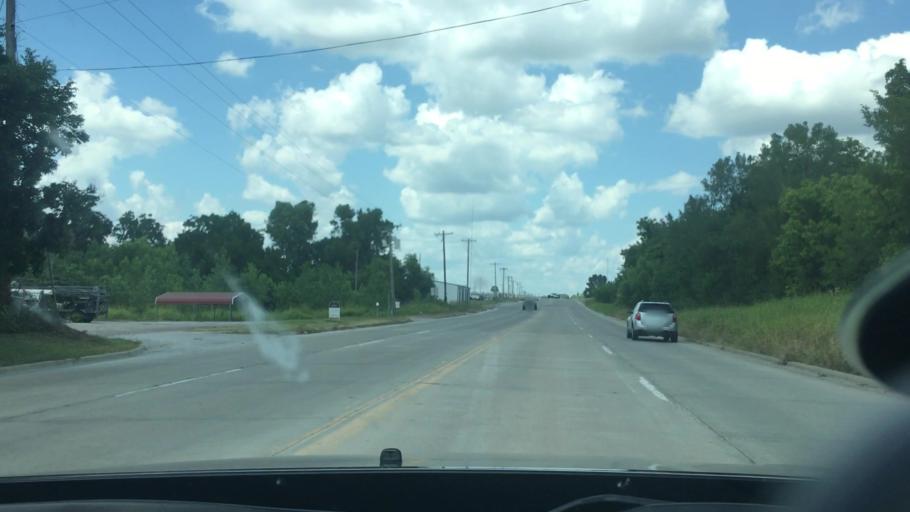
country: US
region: Oklahoma
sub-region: Pontotoc County
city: Ada
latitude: 34.7658
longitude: -96.7005
